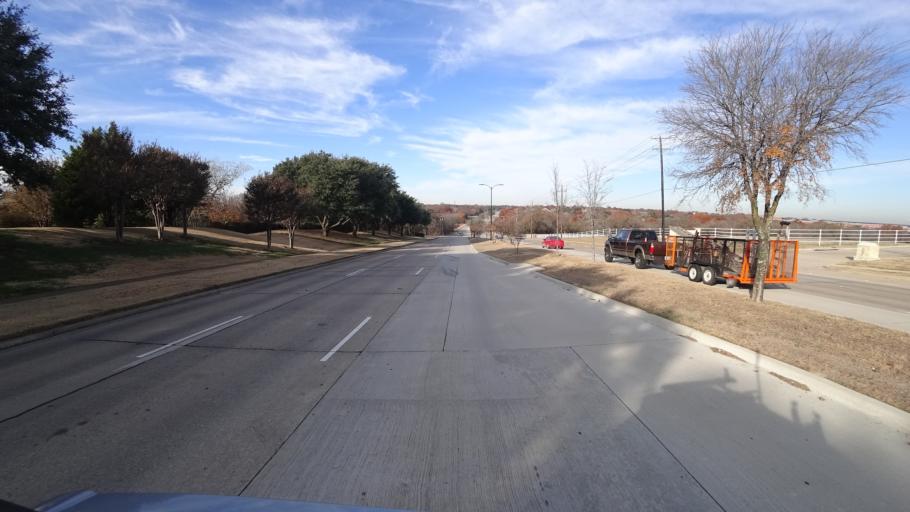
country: US
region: Texas
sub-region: Collin County
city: Fairview
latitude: 33.1967
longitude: -96.6732
